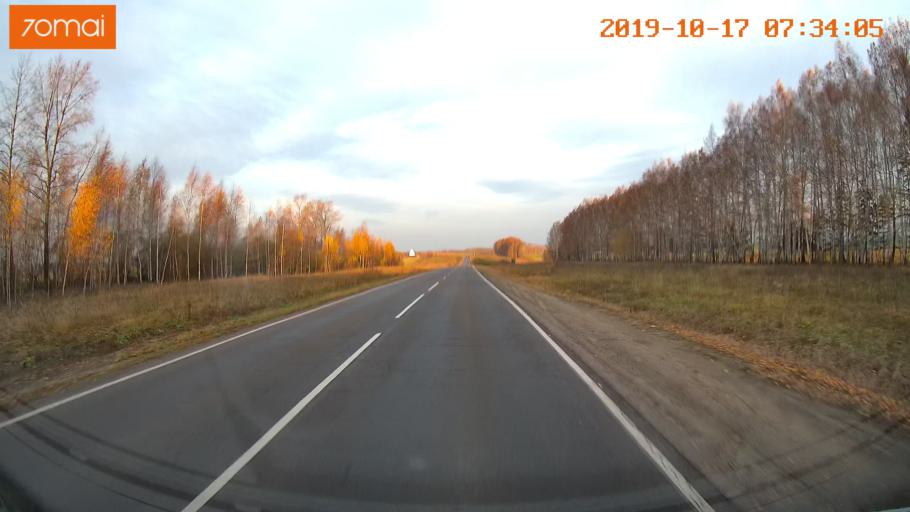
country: RU
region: Ivanovo
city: Gavrilov Posad
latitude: 56.4146
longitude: 39.9491
